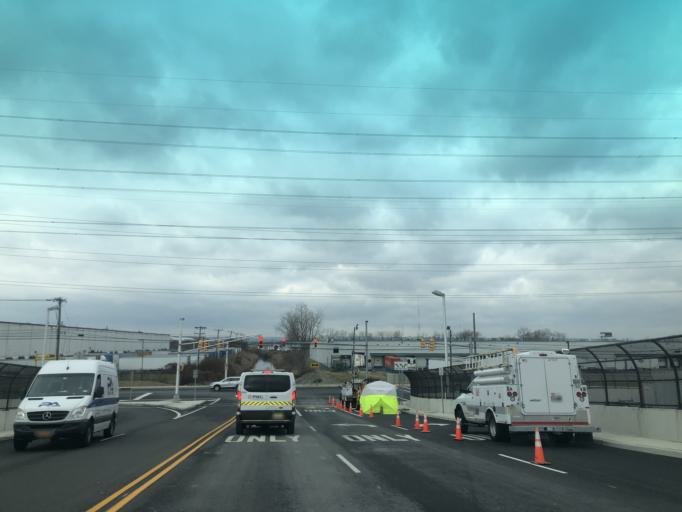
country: US
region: New Jersey
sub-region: Hudson County
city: North Bergen
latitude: 40.8016
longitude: -74.0259
